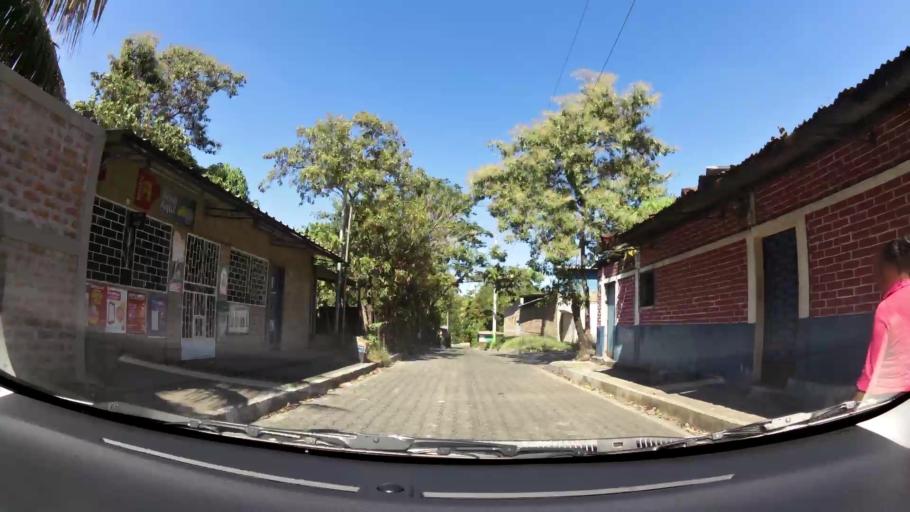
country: SV
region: Sonsonate
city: Armenia
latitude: 13.7322
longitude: -89.3837
